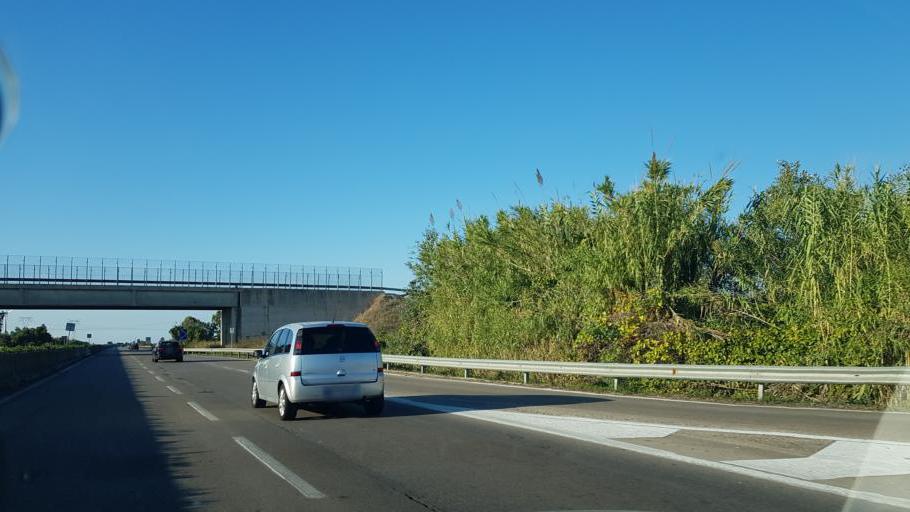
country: IT
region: Apulia
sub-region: Provincia di Brindisi
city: Tuturano
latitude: 40.5531
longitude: 17.9951
